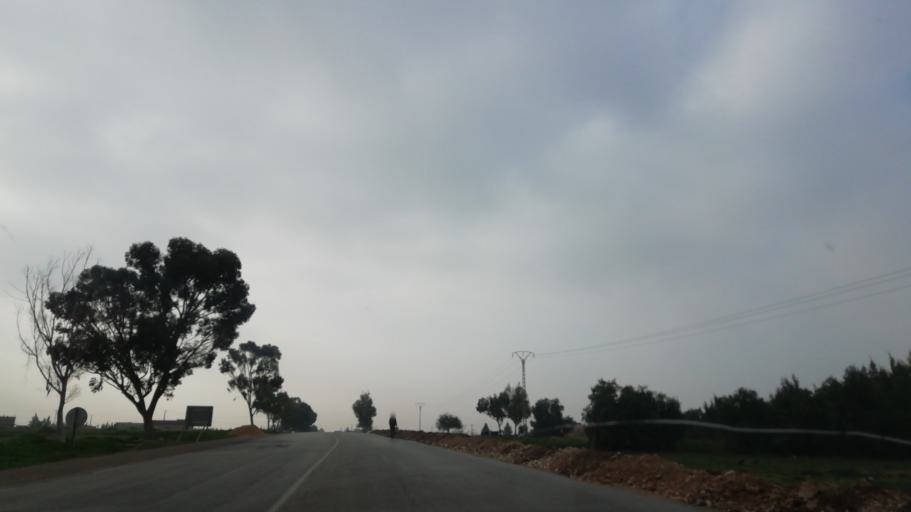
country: DZ
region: Relizane
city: Djidiouia
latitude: 35.8893
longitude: 0.7339
